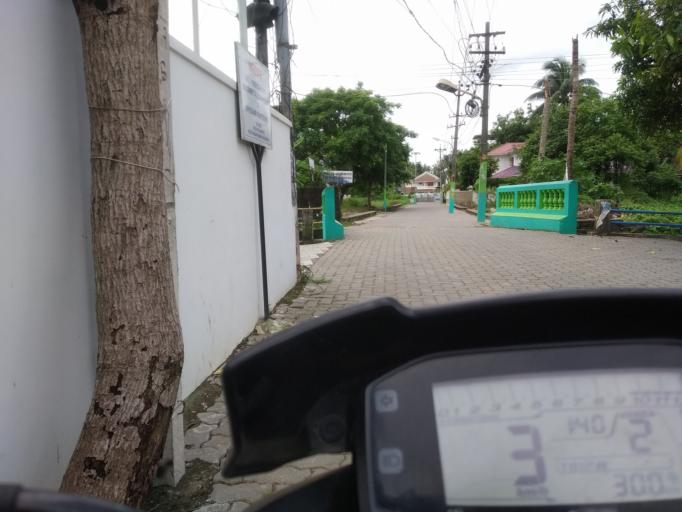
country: IN
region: Kerala
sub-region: Ernakulam
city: Elur
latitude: 10.0131
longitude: 76.2956
